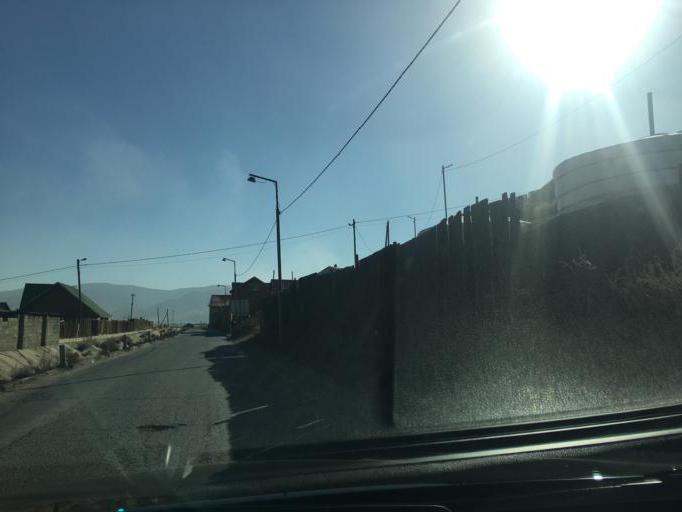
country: MN
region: Ulaanbaatar
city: Ulaanbaatar
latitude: 47.9360
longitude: 106.8822
